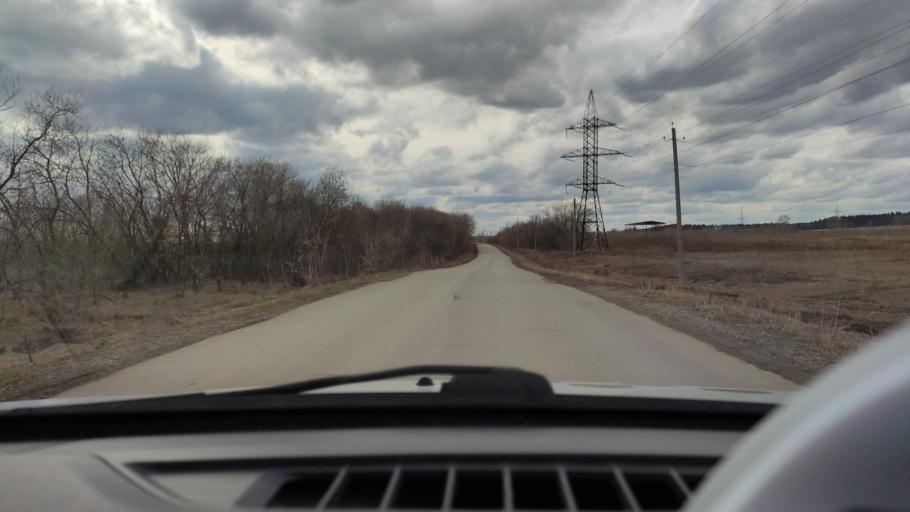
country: RU
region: Perm
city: Froly
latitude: 57.9298
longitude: 56.2495
